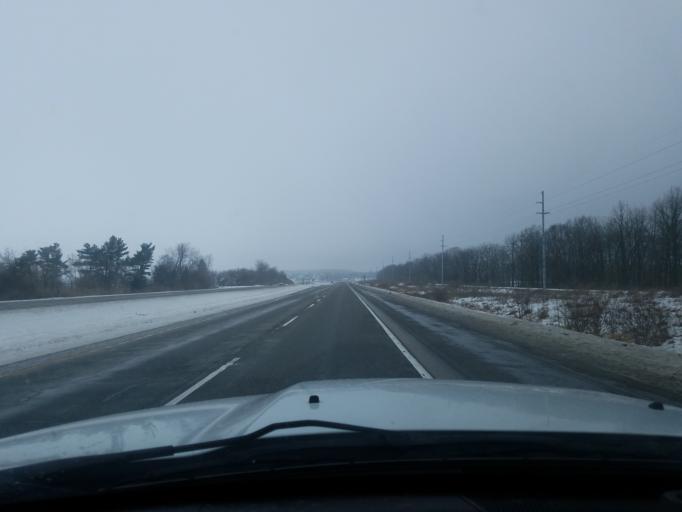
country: US
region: Indiana
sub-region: Fulton County
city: Rochester
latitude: 41.0259
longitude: -86.1796
